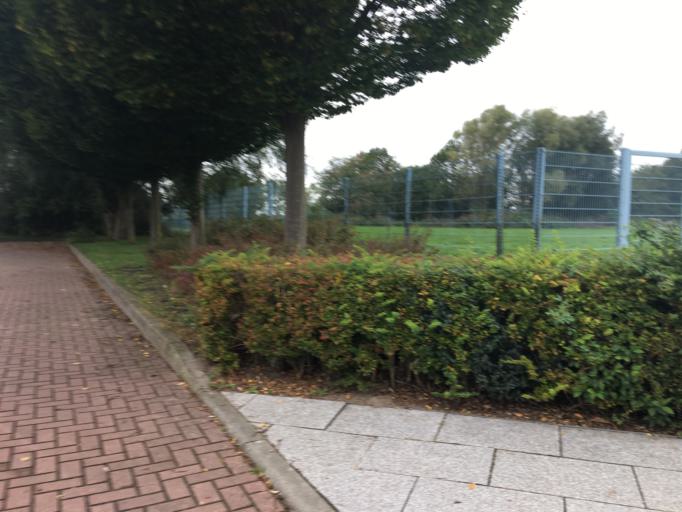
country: DE
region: Mecklenburg-Vorpommern
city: Kramerhof
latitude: 54.3186
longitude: 13.0433
